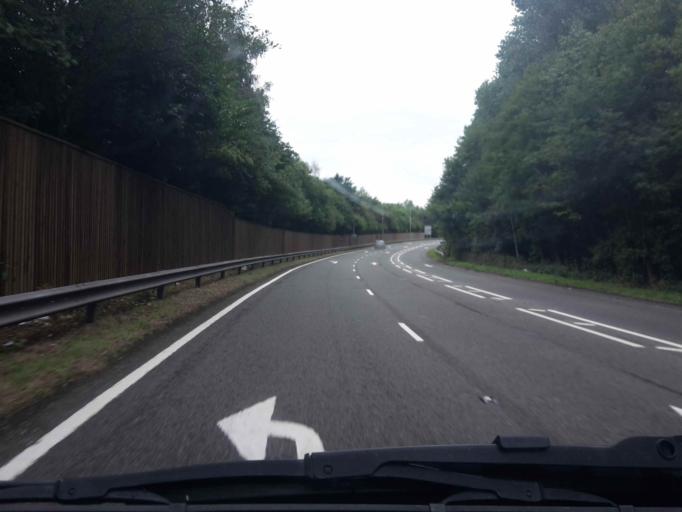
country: GB
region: England
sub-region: Hampshire
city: Fleet
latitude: 51.2955
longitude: -0.7990
